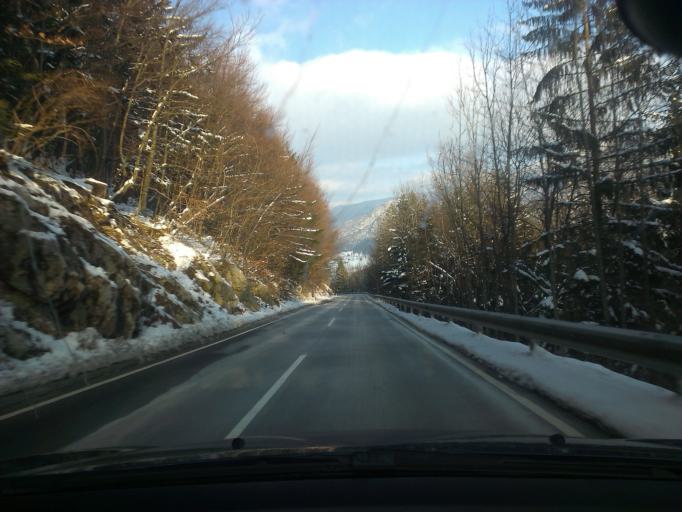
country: AT
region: Lower Austria
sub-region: Politischer Bezirk Wiener Neustadt
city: Miesenbach
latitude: 47.8198
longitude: 15.9505
